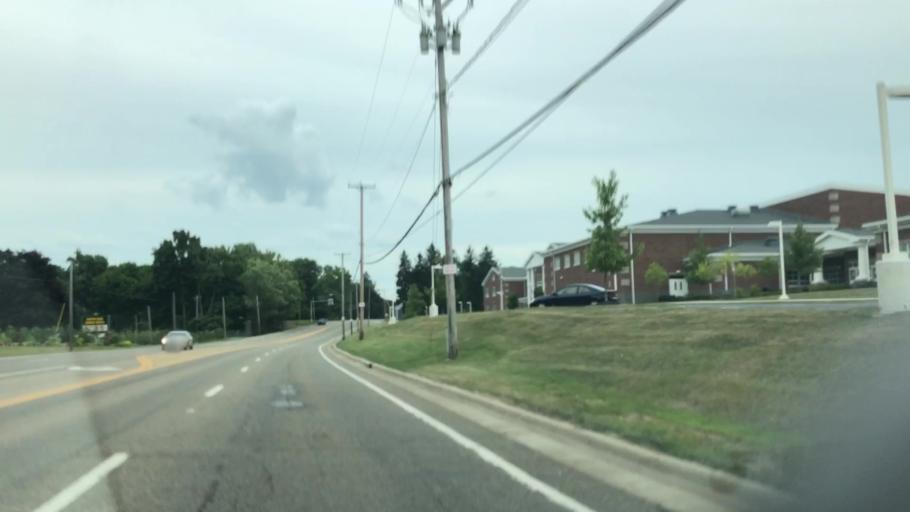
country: US
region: Ohio
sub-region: Summit County
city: Lakemore
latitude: 41.0183
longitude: -81.4147
